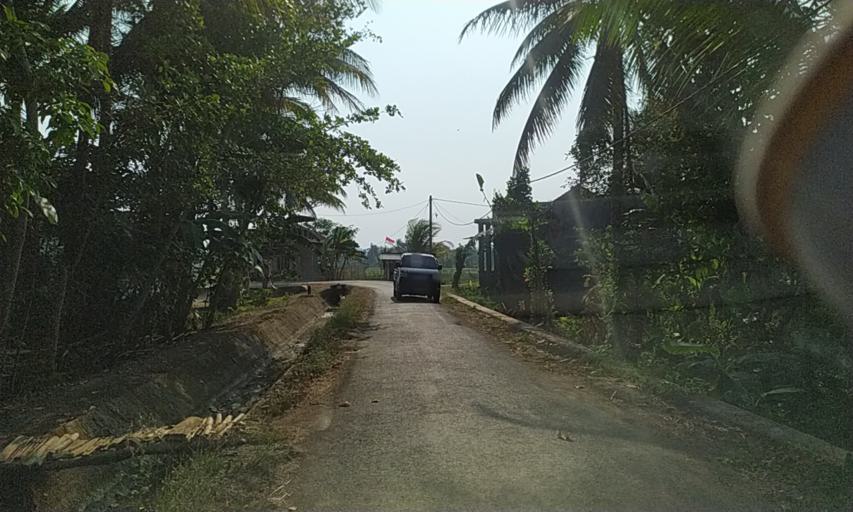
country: ID
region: Central Java
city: Mulyadadi
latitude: -7.3429
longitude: 108.7542
